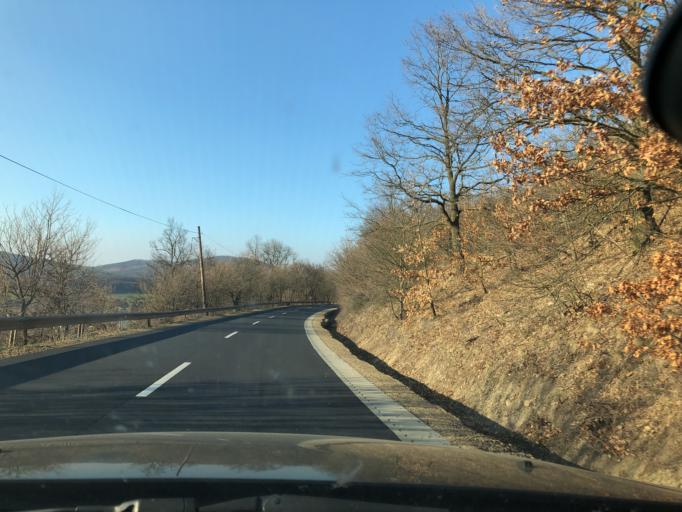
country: HU
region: Nograd
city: Bujak
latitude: 47.9421
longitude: 19.5987
